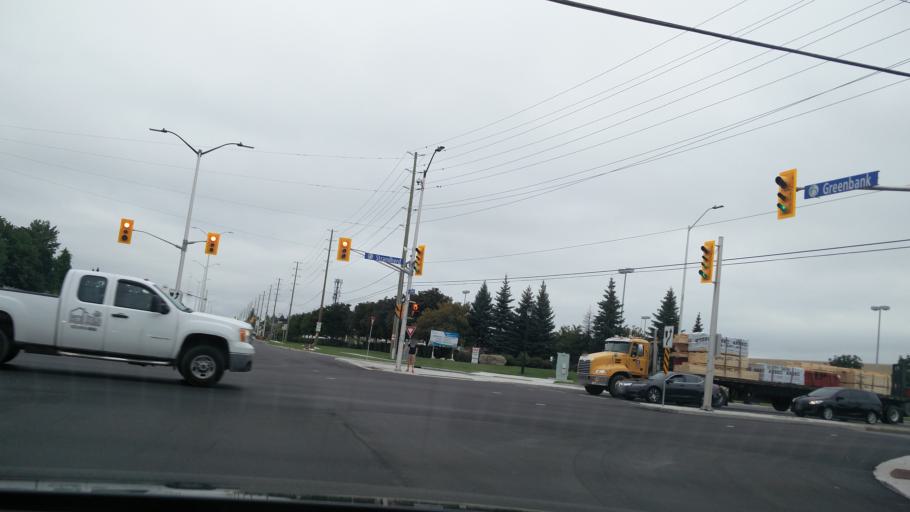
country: CA
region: Ontario
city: Bells Corners
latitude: 45.2704
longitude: -75.7463
